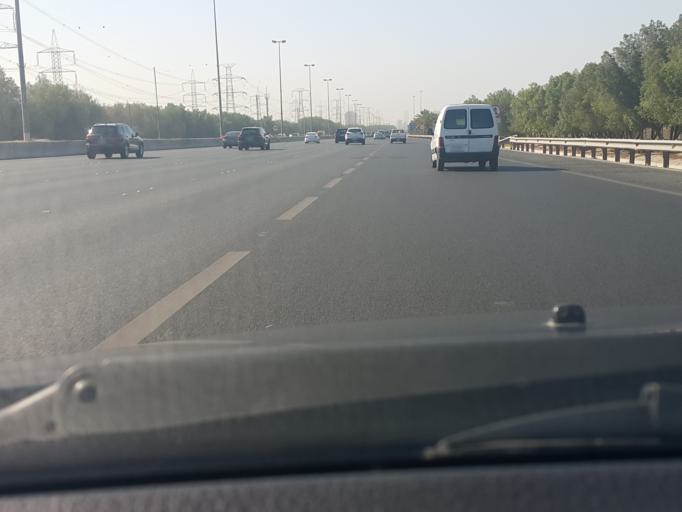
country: KW
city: Bayan
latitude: 29.2843
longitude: 48.0330
